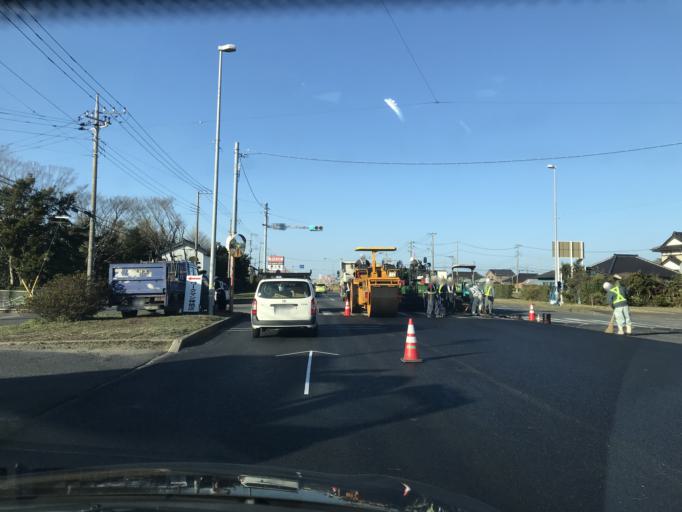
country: JP
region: Ibaraki
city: Kashima-shi
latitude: 35.9084
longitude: 140.6359
